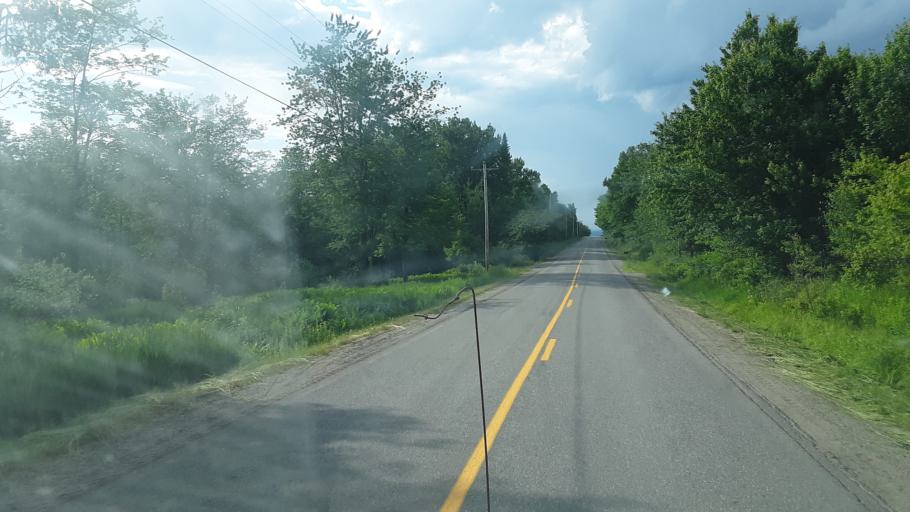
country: US
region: Maine
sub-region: Washington County
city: Calais
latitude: 45.0881
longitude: -67.5035
